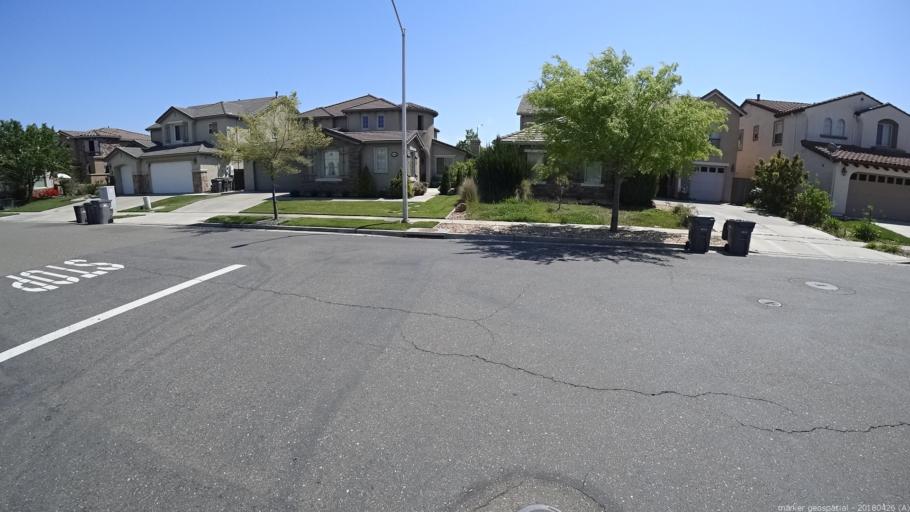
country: US
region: California
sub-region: Yolo County
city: West Sacramento
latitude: 38.5260
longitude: -121.5709
